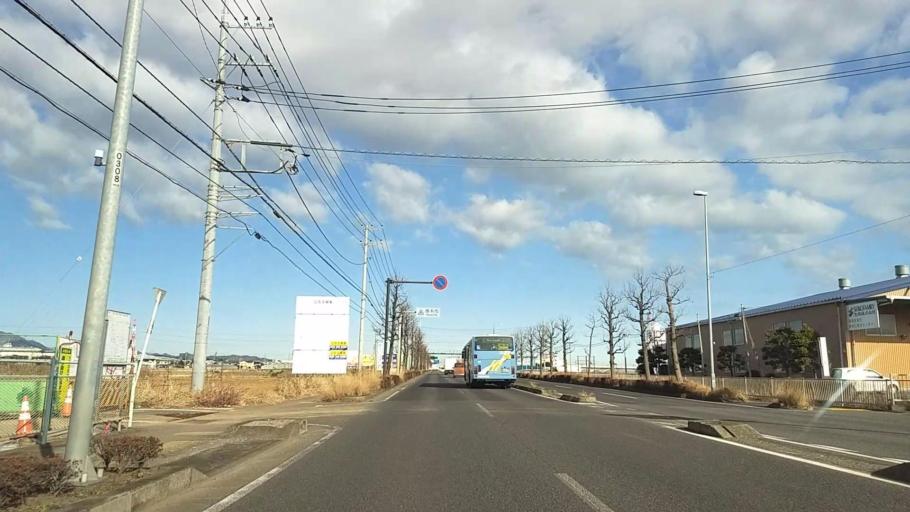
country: JP
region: Kanagawa
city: Atsugi
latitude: 35.3947
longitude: 139.3616
